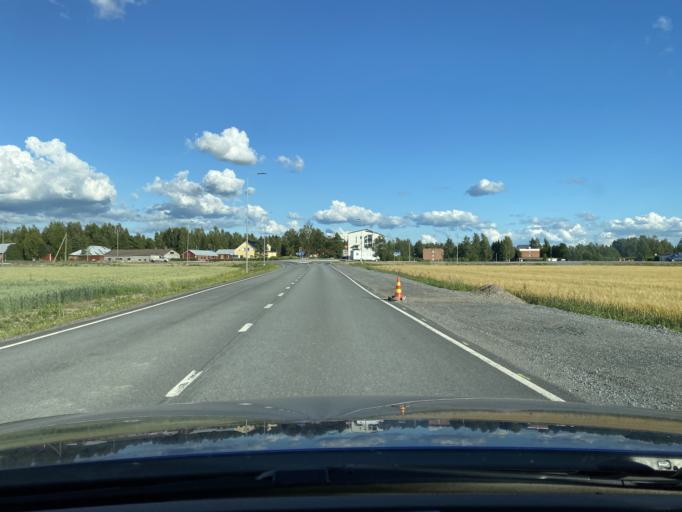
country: FI
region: Ostrobothnia
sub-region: Kyroenmaa
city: Laihia
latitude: 62.9845
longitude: 22.0048
